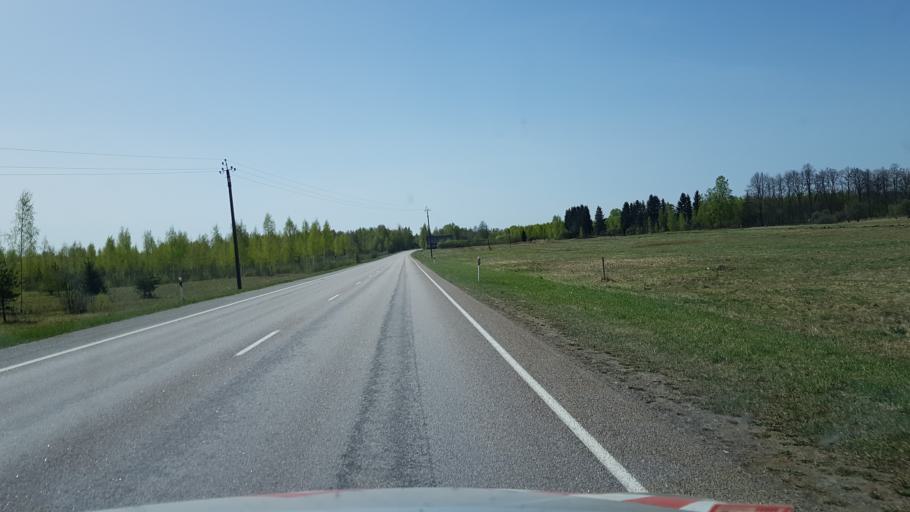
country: EE
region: Valgamaa
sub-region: Valga linn
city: Valga
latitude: 57.8124
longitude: 26.0420
